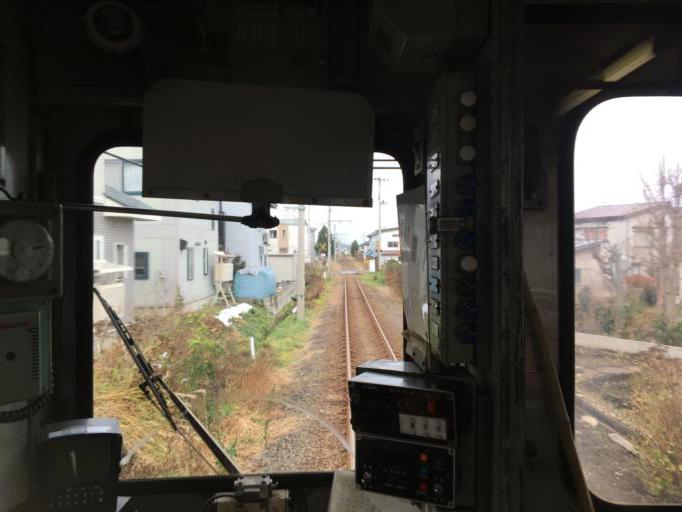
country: JP
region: Aomori
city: Hirosaki
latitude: 40.5706
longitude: 140.4766
